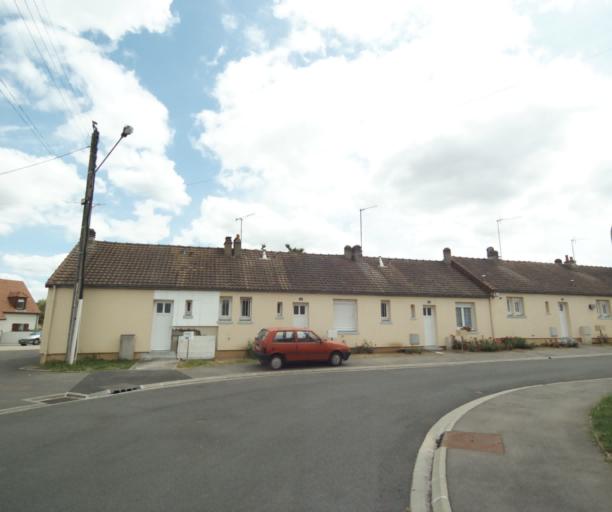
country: FR
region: Centre
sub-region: Departement d'Eure-et-Loir
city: Luce
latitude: 48.4435
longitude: 1.4630
